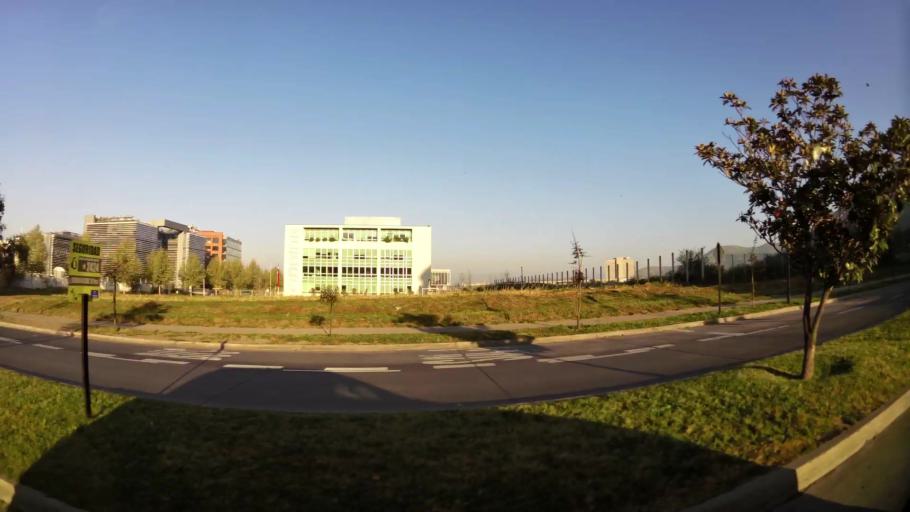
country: CL
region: Santiago Metropolitan
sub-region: Provincia de Santiago
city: Santiago
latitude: -33.3862
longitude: -70.6149
